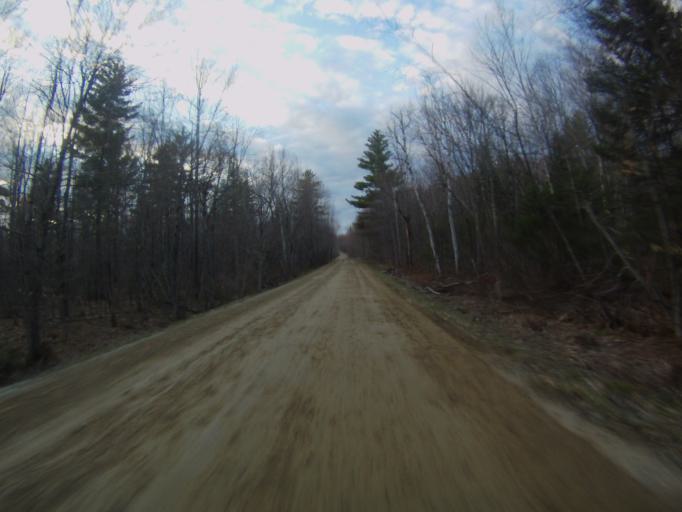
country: US
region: Vermont
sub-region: Rutland County
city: Brandon
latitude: 43.9041
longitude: -73.0160
